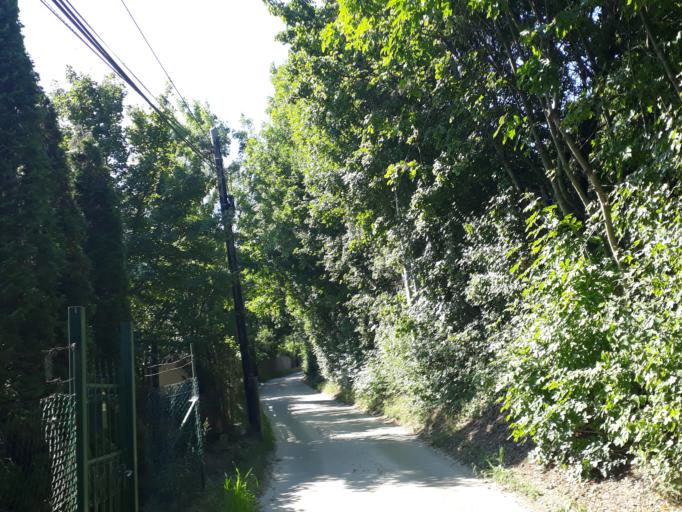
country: HU
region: Pest
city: Budaors
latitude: 47.4804
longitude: 18.9780
